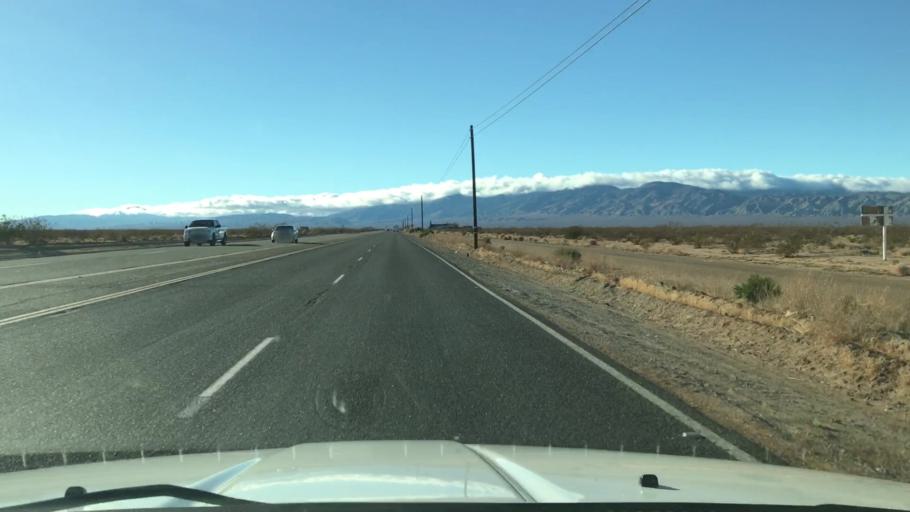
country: US
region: California
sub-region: Kern County
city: California City
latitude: 35.1258
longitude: -118.0150
